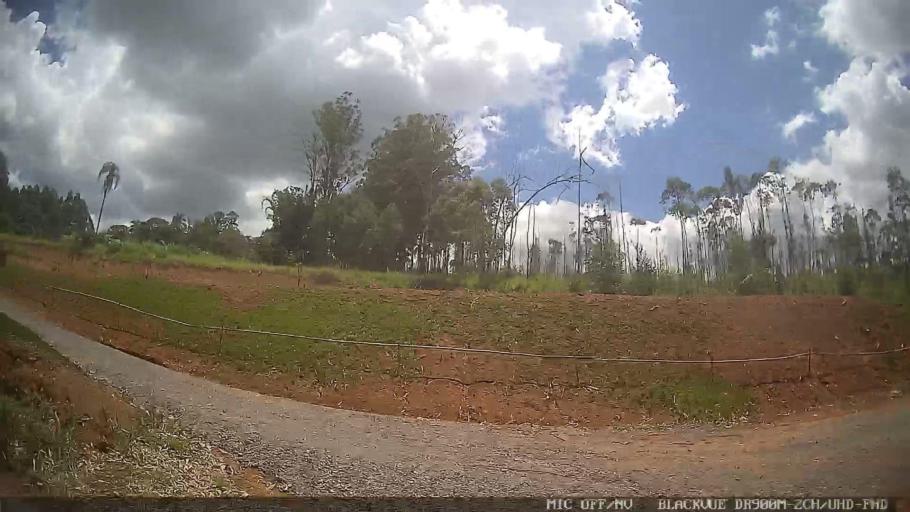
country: BR
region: Sao Paulo
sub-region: Braganca Paulista
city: Braganca Paulista
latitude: -22.9961
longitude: -46.4556
